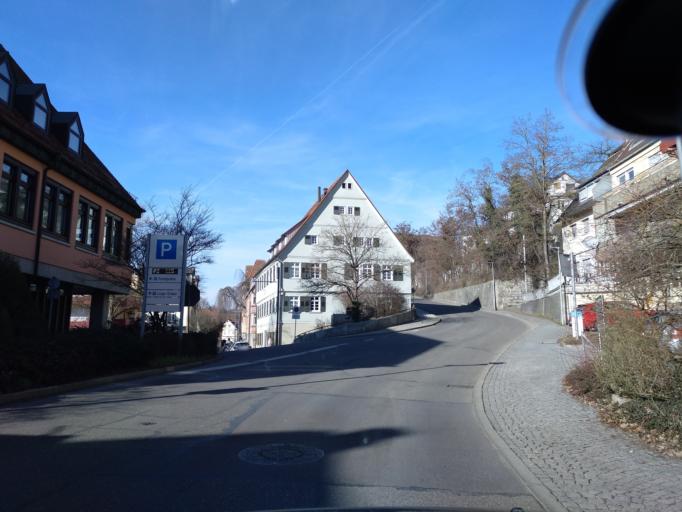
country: DE
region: Baden-Wuerttemberg
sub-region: Regierungsbezirk Stuttgart
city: Schwaebisch Hall
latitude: 49.1089
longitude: 9.7398
